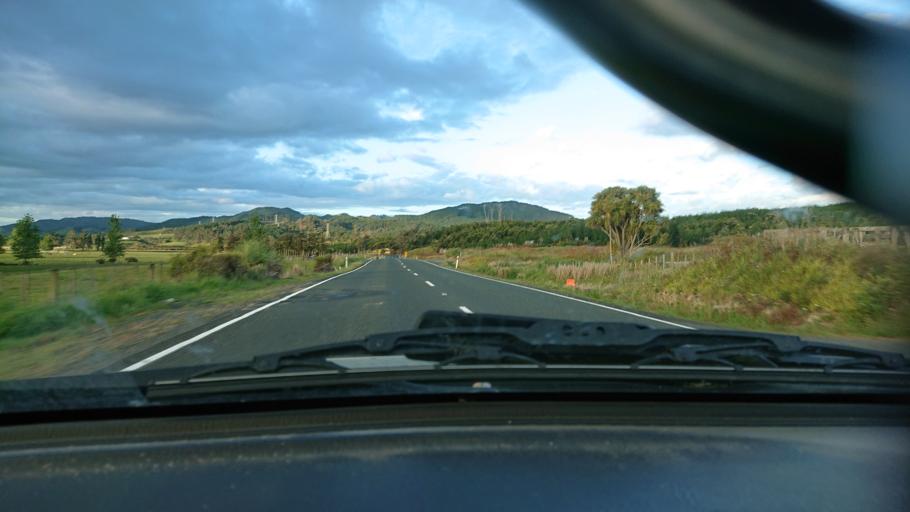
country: NZ
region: Auckland
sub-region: Auckland
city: Parakai
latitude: -36.5168
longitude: 174.4506
